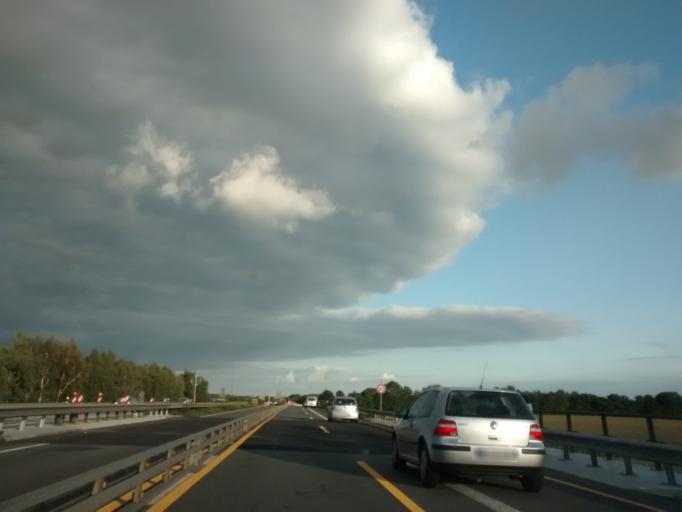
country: DE
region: Lower Saxony
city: Salzbergen
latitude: 52.3387
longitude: 7.2887
